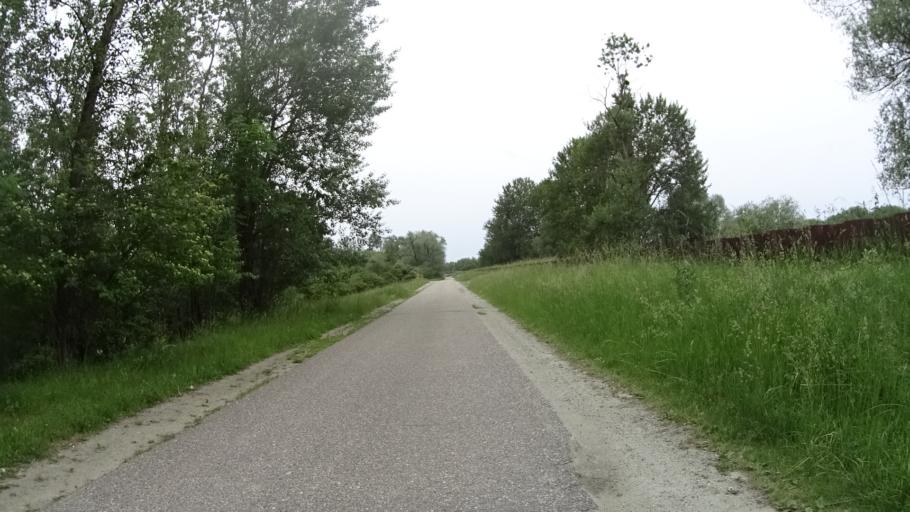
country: DE
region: Bavaria
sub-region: Lower Bavaria
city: Niederalteich
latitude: 48.7796
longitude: 13.0081
